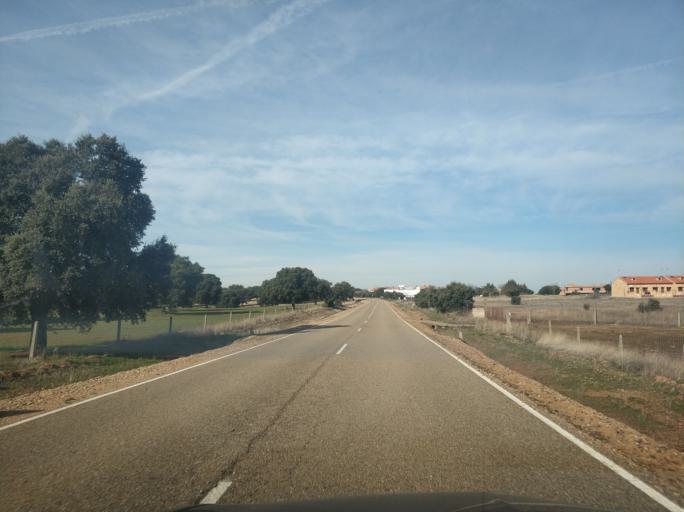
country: ES
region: Castille and Leon
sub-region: Provincia de Salamanca
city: Zarapicos
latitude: 41.0077
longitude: -5.8408
